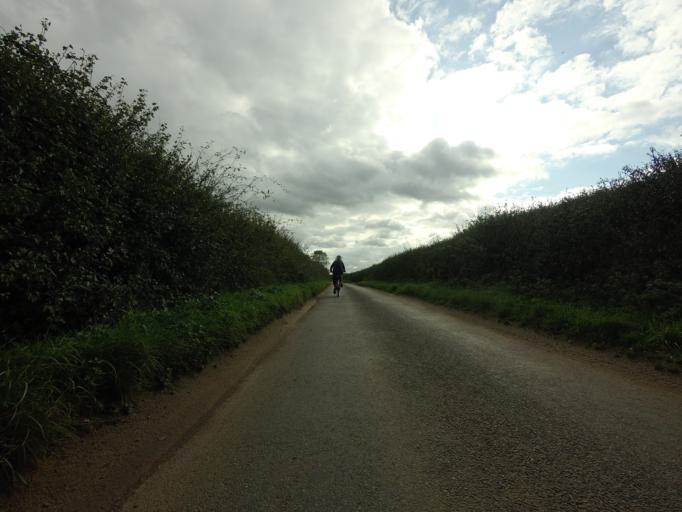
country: GB
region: England
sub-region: Norfolk
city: Snettisham
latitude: 52.8746
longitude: 0.5140
